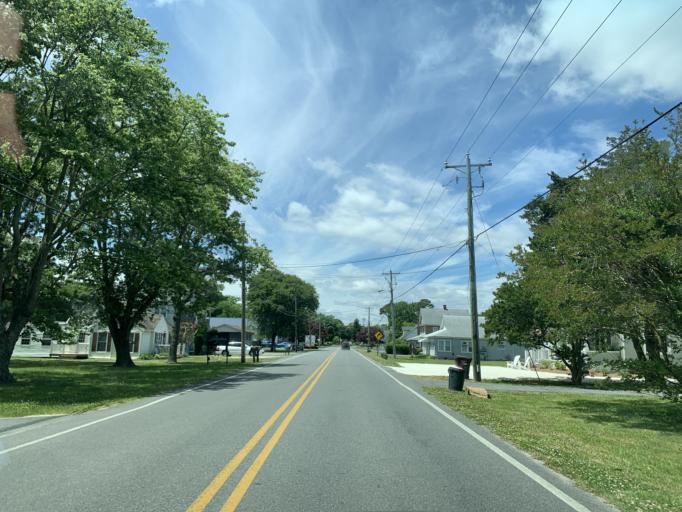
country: US
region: Maryland
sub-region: Worcester County
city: West Ocean City
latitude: 38.3322
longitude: -75.1100
